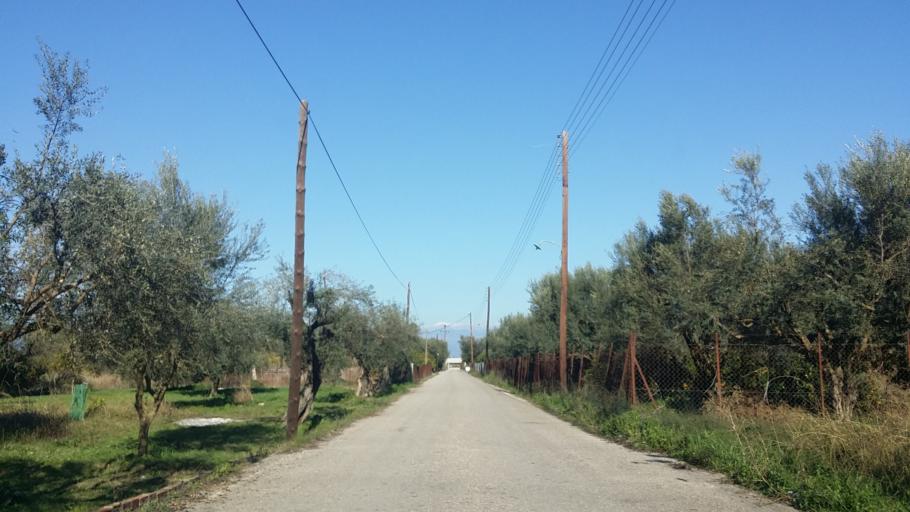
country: GR
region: West Greece
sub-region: Nomos Achaias
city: Temeni
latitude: 38.1907
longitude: 22.1816
